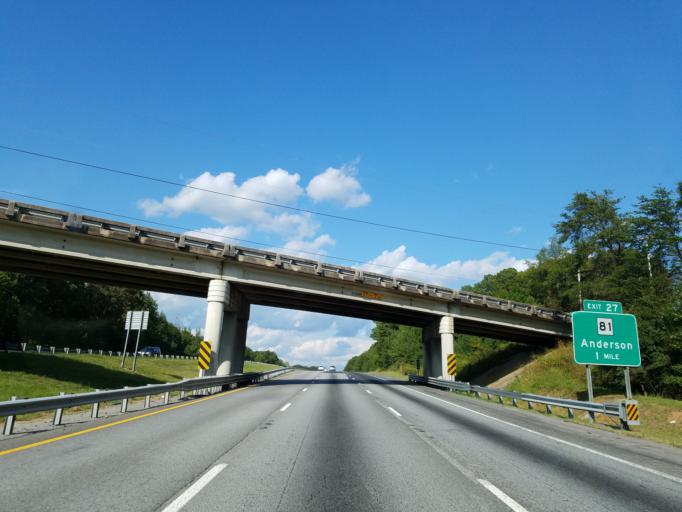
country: US
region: South Carolina
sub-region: Anderson County
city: Northlake
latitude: 34.6221
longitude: -82.6159
